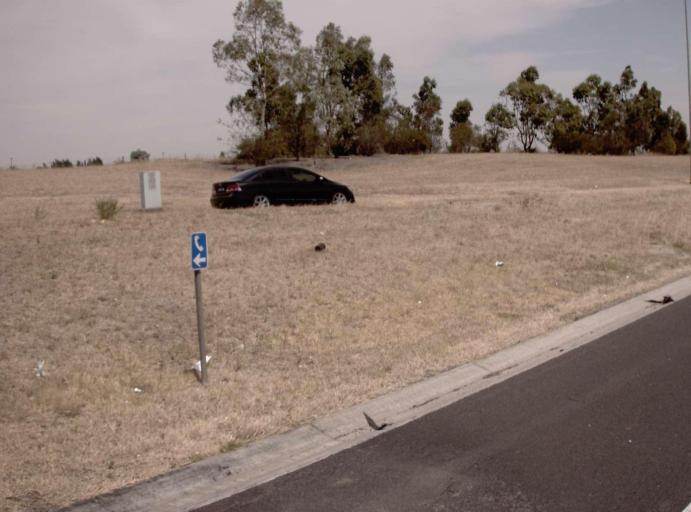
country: AU
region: Victoria
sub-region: Moonee Valley
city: Keilor East
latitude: -37.7404
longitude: 144.8494
